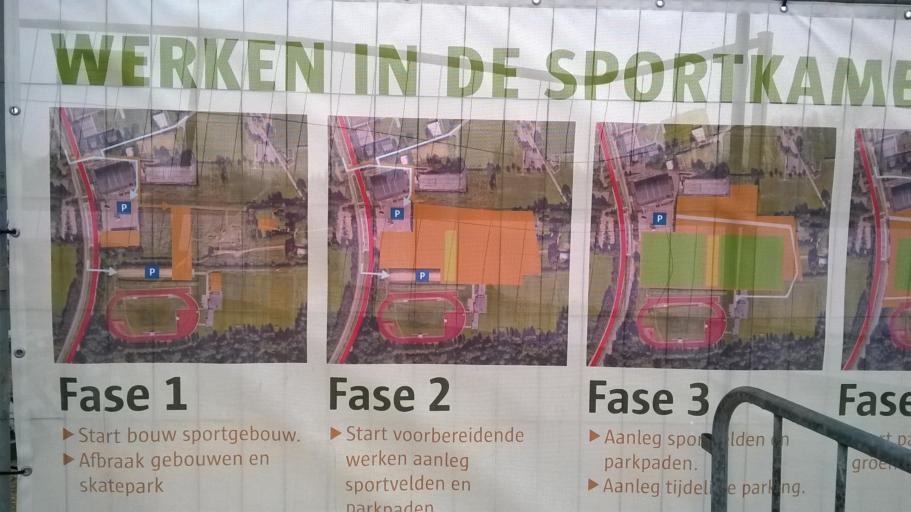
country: BE
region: Flanders
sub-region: Provincie Antwerpen
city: Borsbeek
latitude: 51.2159
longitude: 4.4842
